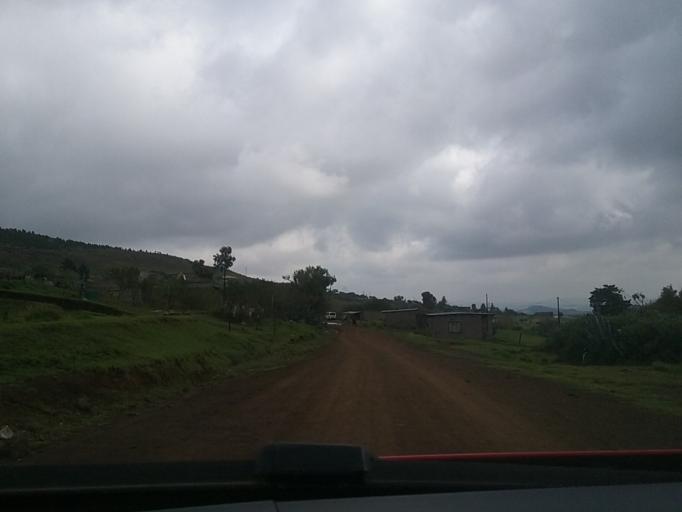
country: LS
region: Berea
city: Teyateyaneng
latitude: -29.2492
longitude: 27.8443
